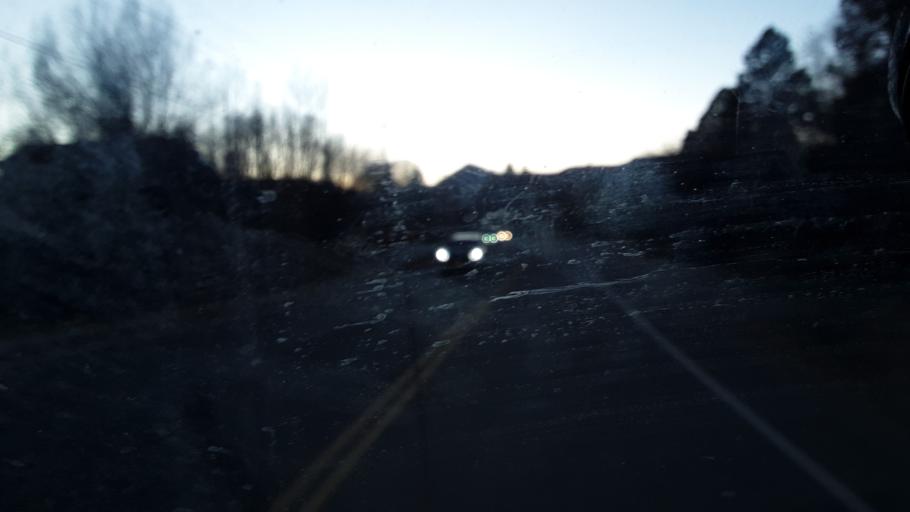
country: US
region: Colorado
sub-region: La Plata County
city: Durango
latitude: 37.3039
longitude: -107.8338
